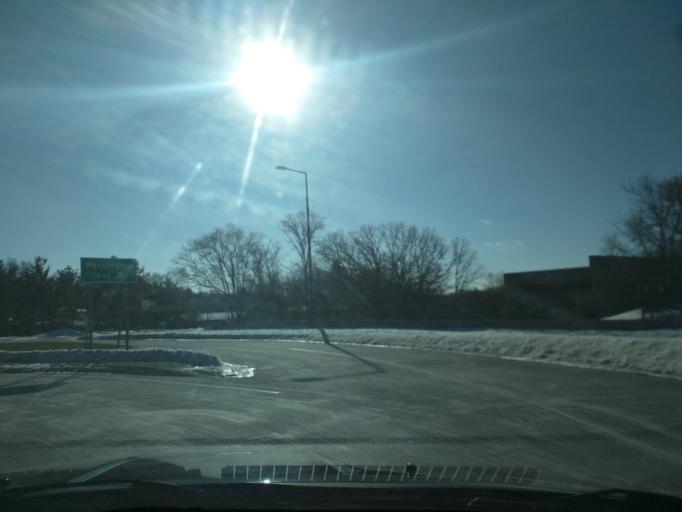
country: US
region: Minnesota
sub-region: Hennepin County
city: Edina
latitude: 44.8586
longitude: -93.3987
